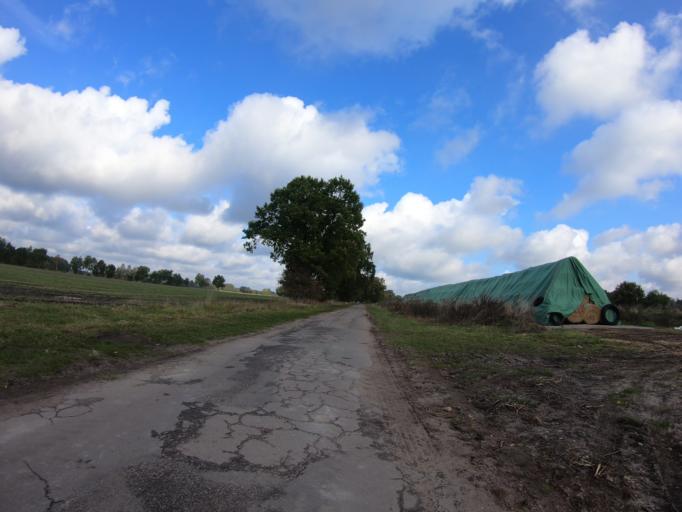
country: DE
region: Lower Saxony
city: Wagenhoff
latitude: 52.5289
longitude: 10.5374
